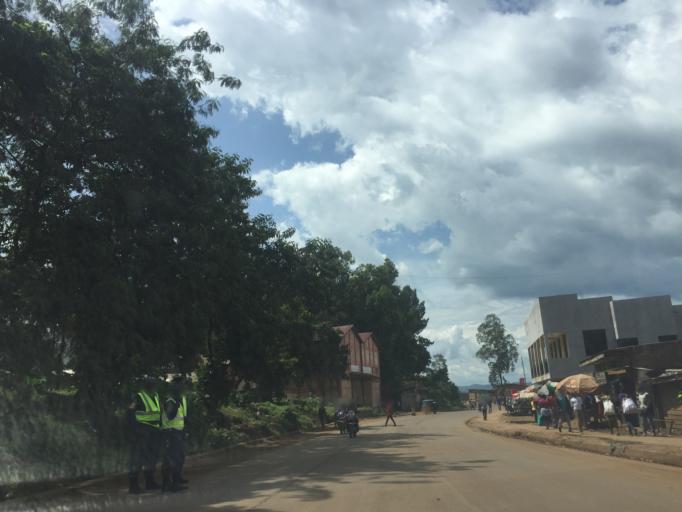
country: CD
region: South Kivu
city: Bukavu
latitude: -2.4914
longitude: 28.8489
